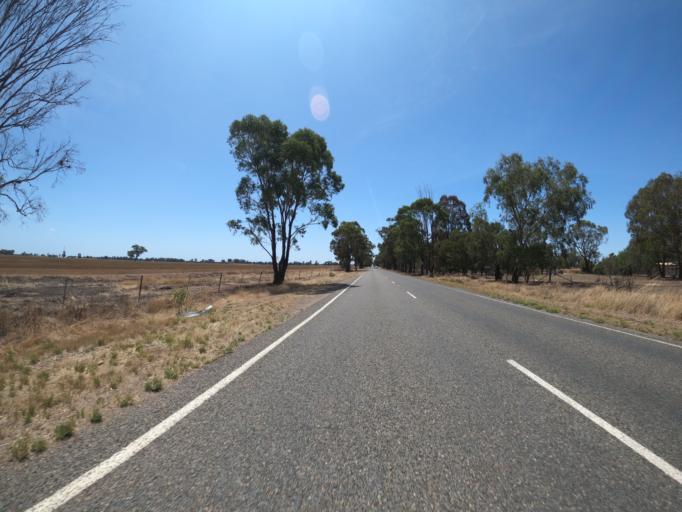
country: AU
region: Victoria
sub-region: Moira
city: Yarrawonga
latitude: -36.0692
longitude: 145.9954
